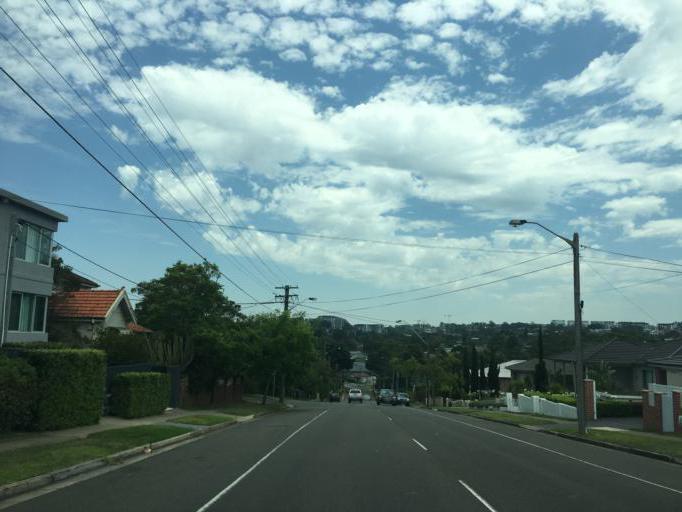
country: AU
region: New South Wales
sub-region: Hunters Hill
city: Gladesville
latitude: -33.8280
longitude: 151.1177
